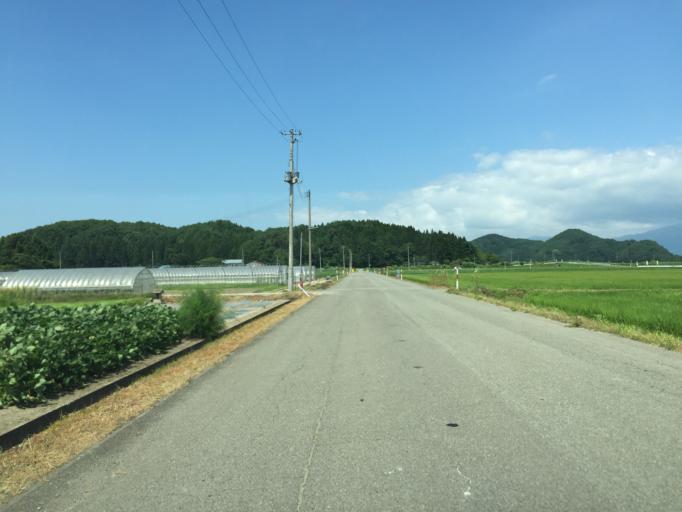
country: JP
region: Fukushima
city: Inawashiro
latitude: 37.4505
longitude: 140.0441
